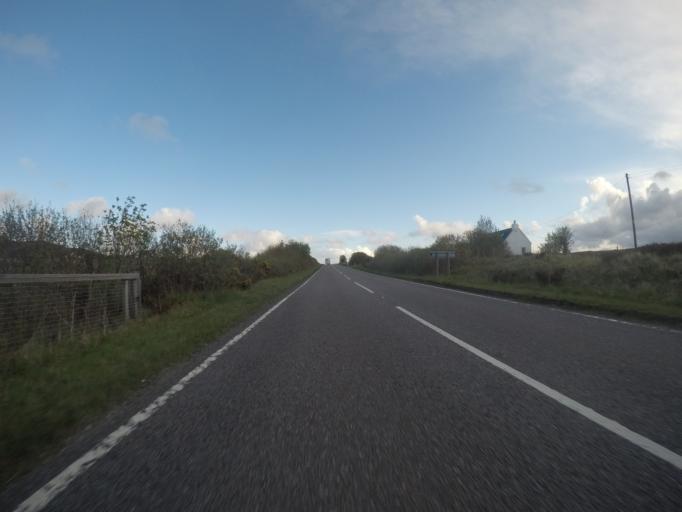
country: GB
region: Scotland
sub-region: Highland
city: Portree
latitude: 57.4780
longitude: -6.3001
